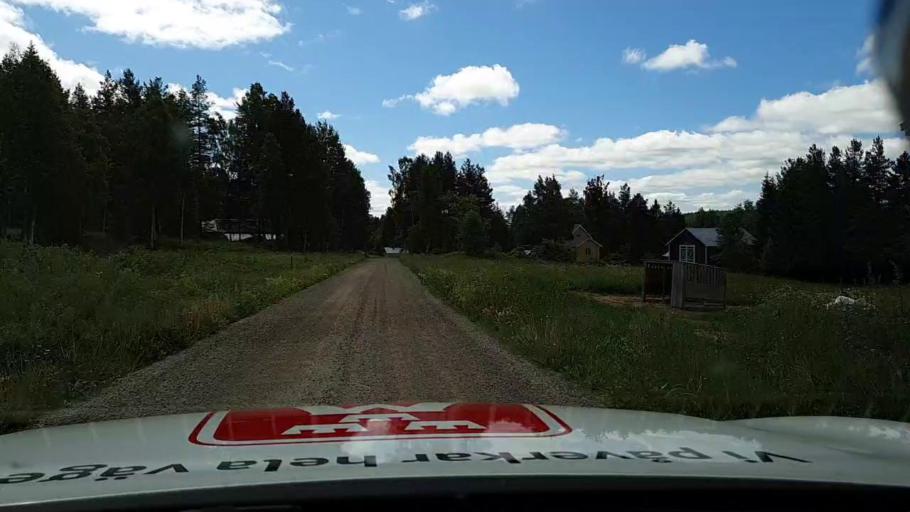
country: SE
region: Jaemtland
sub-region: Braecke Kommun
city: Braecke
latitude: 62.7625
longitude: 15.4994
